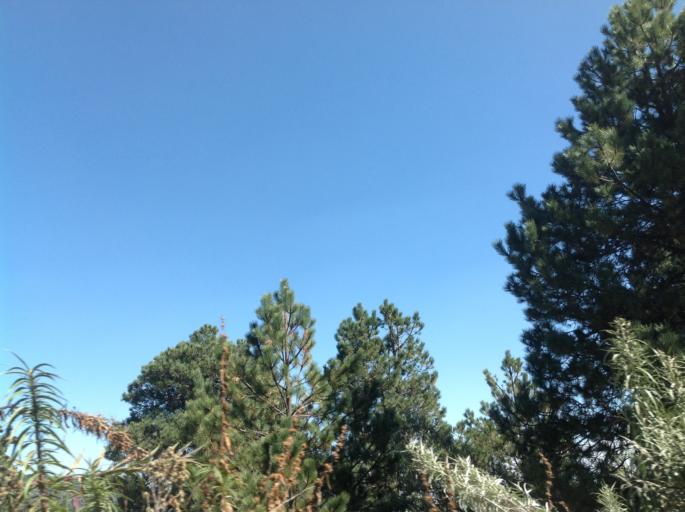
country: MX
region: Mexico
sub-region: Amecameca
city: San Diego Huehuecalco
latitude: 19.1060
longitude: -98.6452
